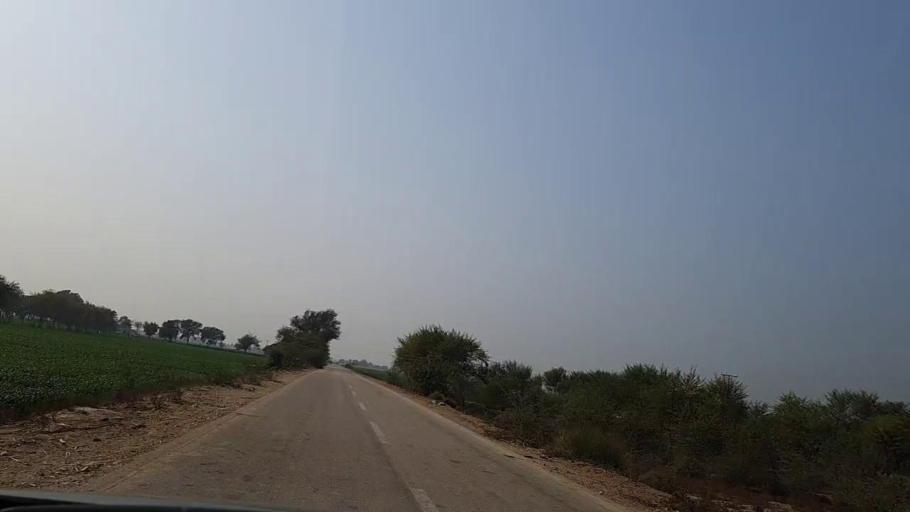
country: PK
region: Sindh
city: Sann
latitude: 26.1395
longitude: 68.1648
